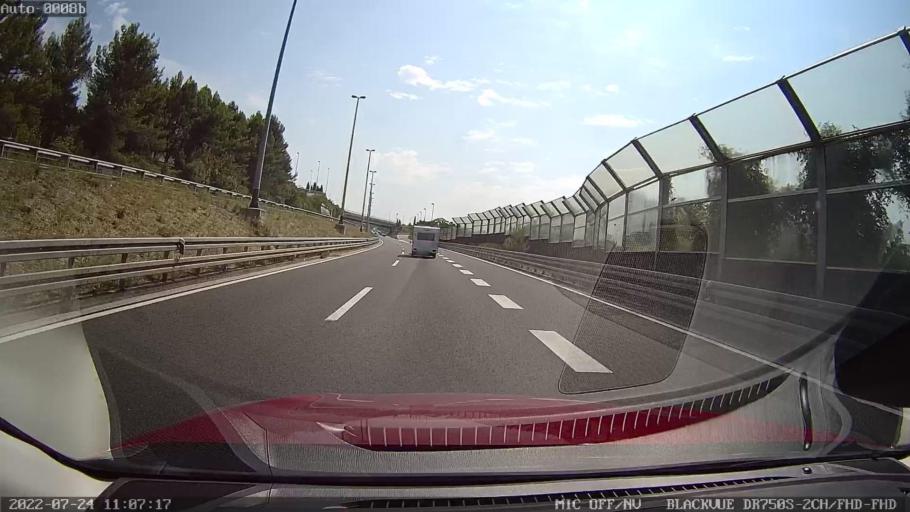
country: HR
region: Primorsko-Goranska
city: Marinici
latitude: 45.3472
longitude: 14.3714
